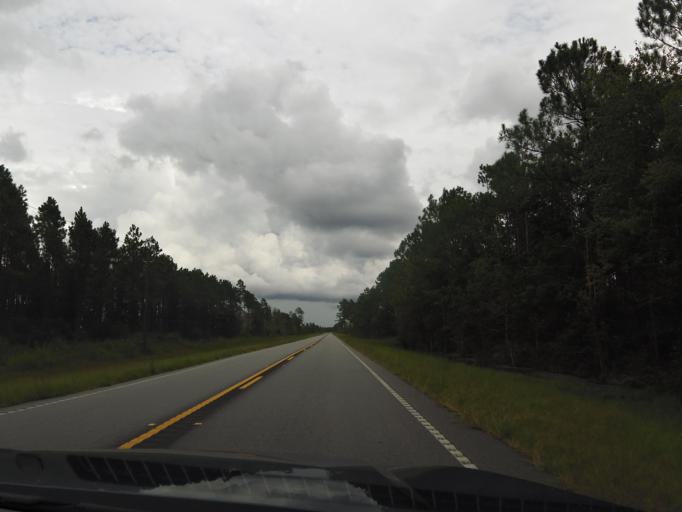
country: US
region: Florida
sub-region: Baker County
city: Macclenny
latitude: 30.5227
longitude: -82.1893
